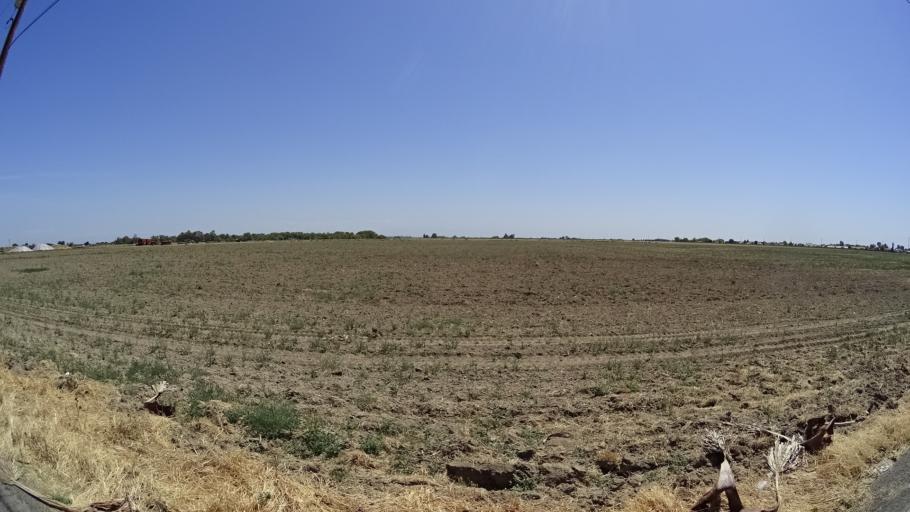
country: US
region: California
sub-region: Kings County
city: Lemoore
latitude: 36.2455
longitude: -119.7628
